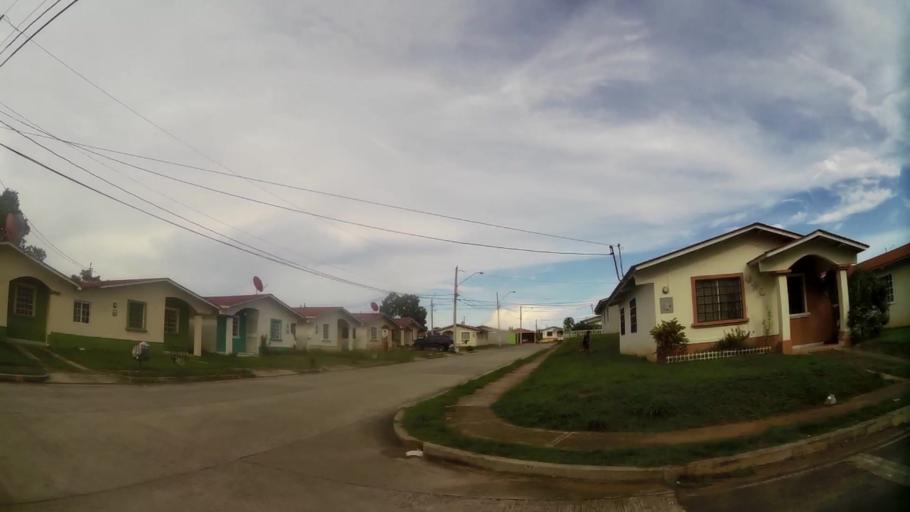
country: PA
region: Panama
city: La Chorrera
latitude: 8.8820
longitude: -79.7680
